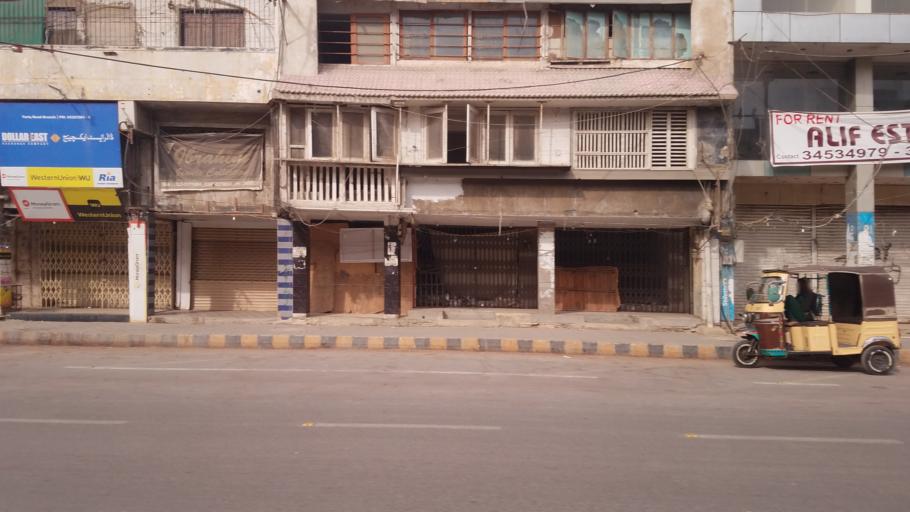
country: PK
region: Sindh
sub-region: Karachi District
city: Karachi
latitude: 24.8725
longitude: 67.0604
